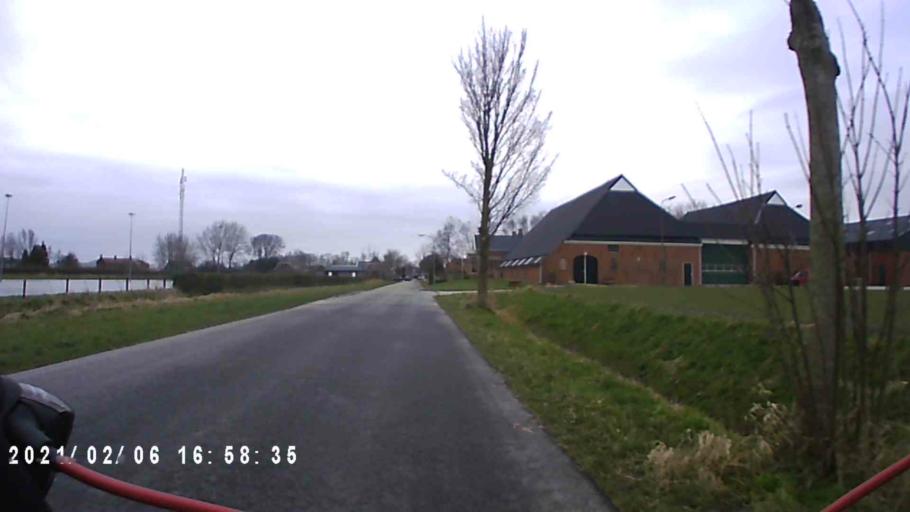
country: NL
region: Groningen
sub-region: Gemeente Appingedam
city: Appingedam
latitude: 53.4171
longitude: 6.7600
